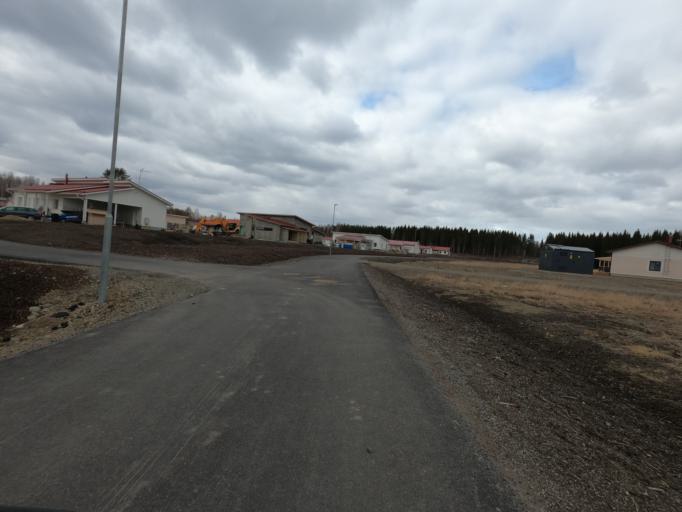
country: FI
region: North Karelia
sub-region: Joensuu
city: Joensuu
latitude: 62.5582
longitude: 29.8249
